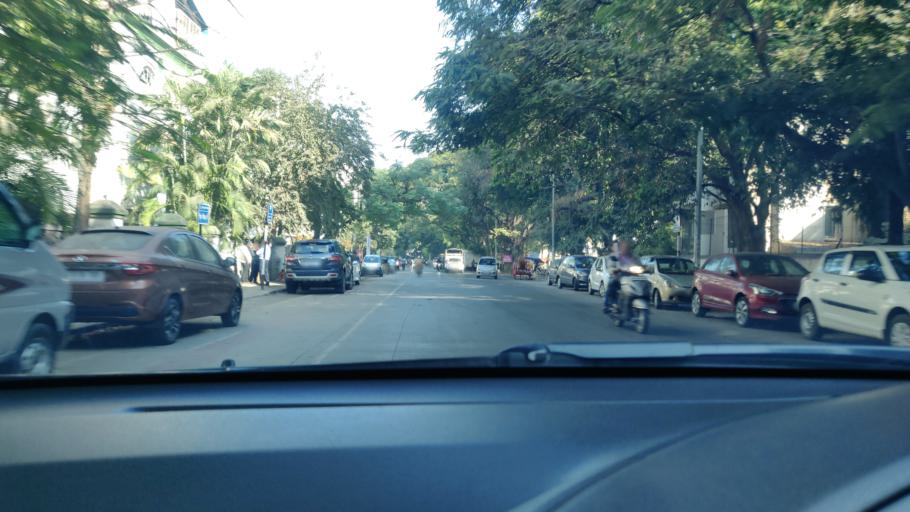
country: IN
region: Maharashtra
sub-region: Pune Division
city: Khadki
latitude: 18.5555
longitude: 73.8047
